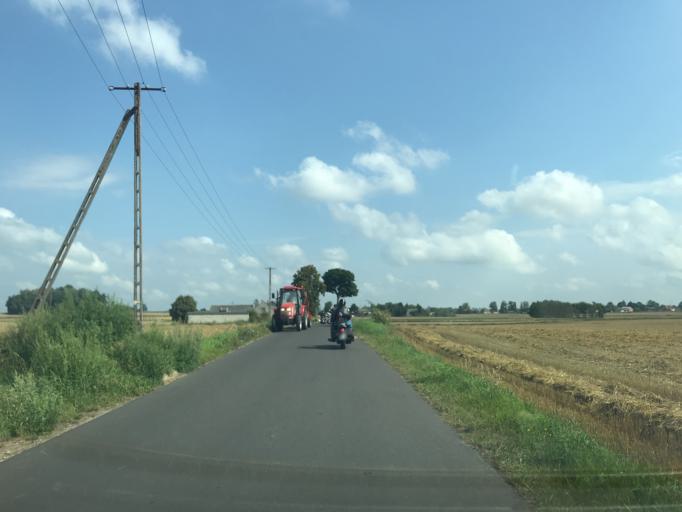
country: PL
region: Warmian-Masurian Voivodeship
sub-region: Powiat nowomiejski
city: Biskupiec
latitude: 53.4589
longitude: 19.4603
